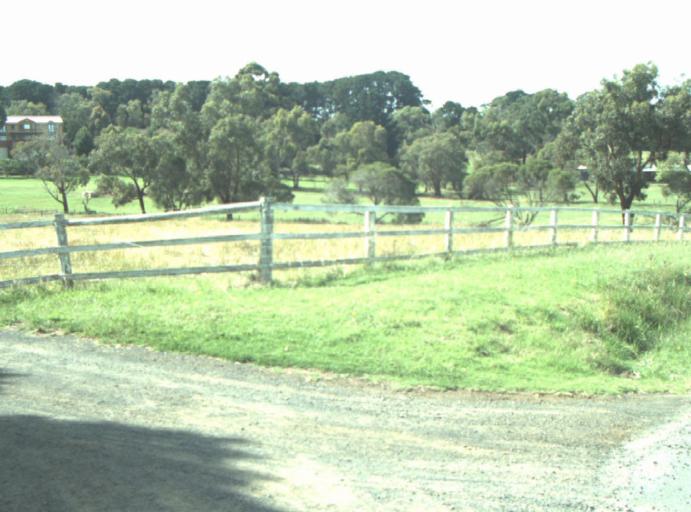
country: AU
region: Victoria
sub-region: Greater Geelong
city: Clifton Springs
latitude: -38.1701
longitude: 144.5592
